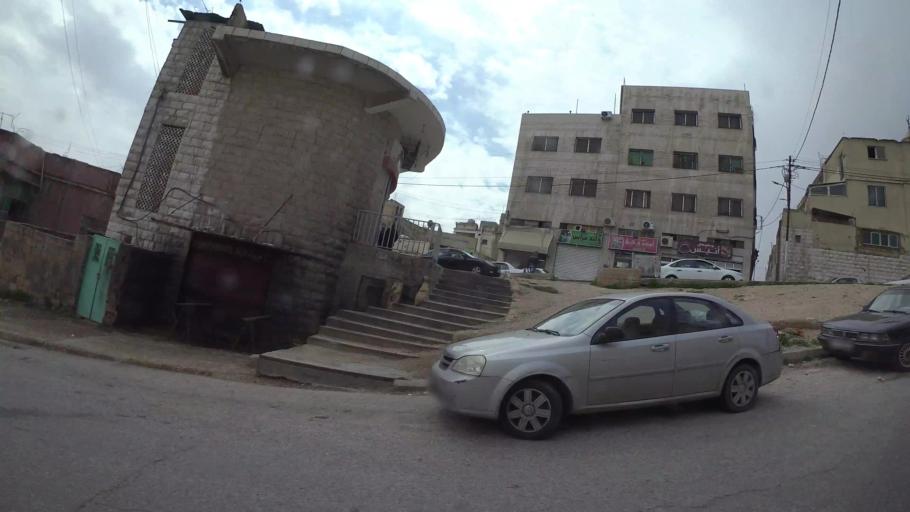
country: JO
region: Amman
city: Amman
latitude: 31.9639
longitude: 35.9299
